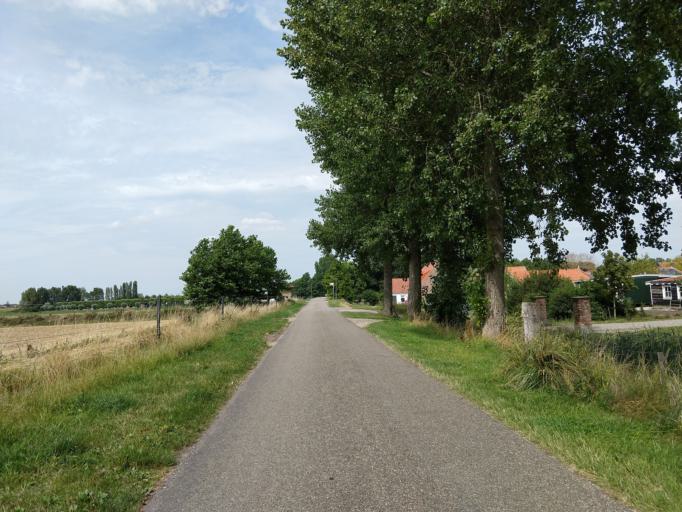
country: NL
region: Zeeland
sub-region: Gemeente Middelburg
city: Middelburg
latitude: 51.4722
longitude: 3.6594
